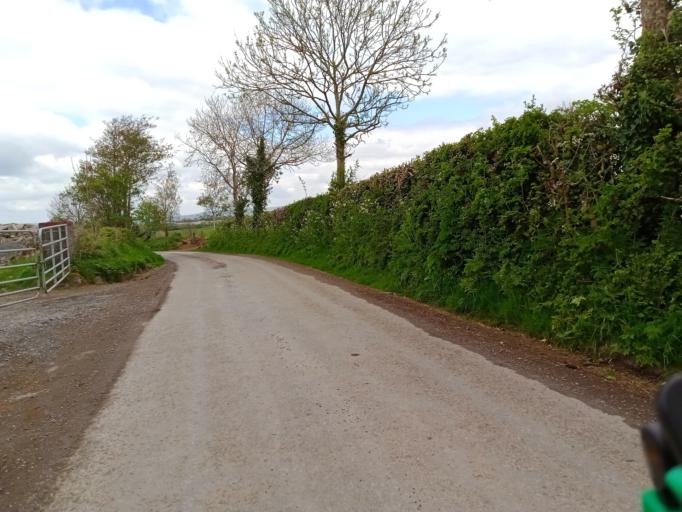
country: IE
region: Leinster
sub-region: Kilkenny
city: Kilkenny
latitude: 52.6253
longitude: -7.2390
